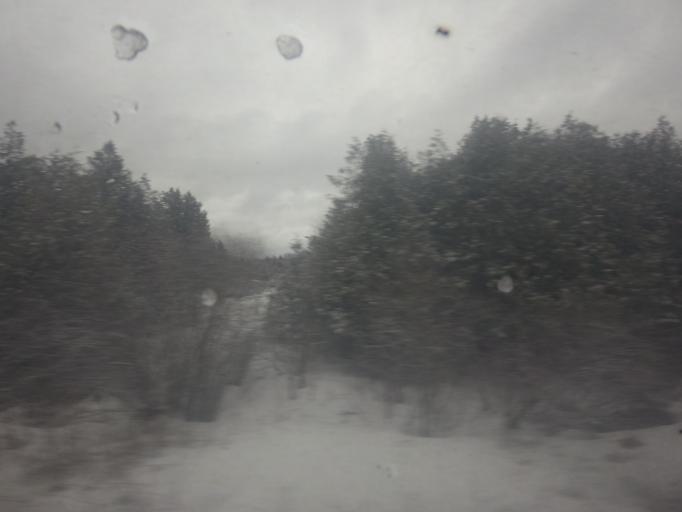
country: CA
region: Ontario
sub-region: Lanark County
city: Smiths Falls
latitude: 44.9549
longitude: -76.0079
